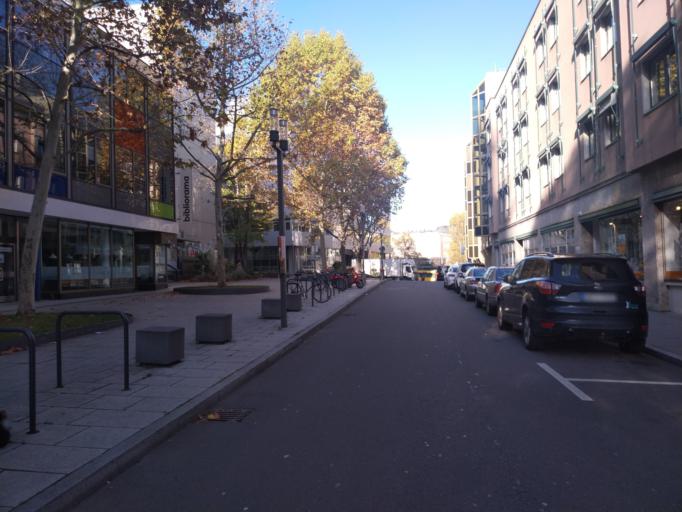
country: DE
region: Baden-Wuerttemberg
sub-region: Regierungsbezirk Stuttgart
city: Stuttgart
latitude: 48.7782
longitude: 9.1723
